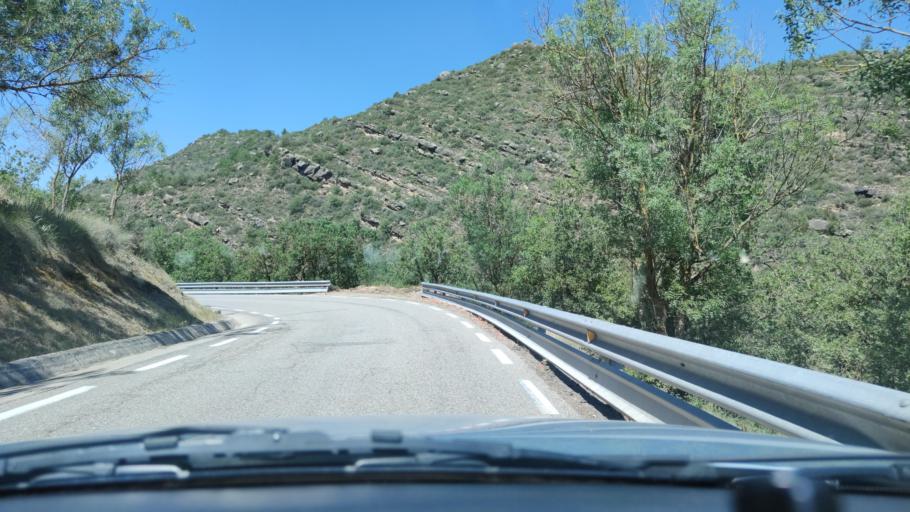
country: ES
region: Catalonia
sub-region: Provincia de Lleida
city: Tora de Riubregos
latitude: 41.8167
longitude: 1.4134
